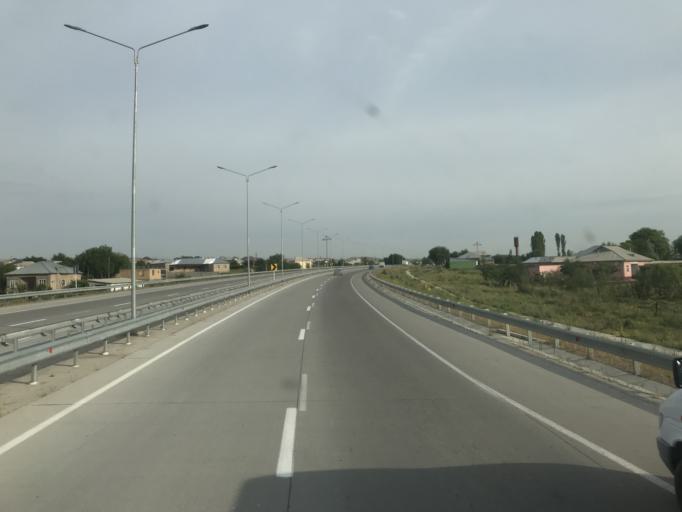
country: KZ
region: Ongtustik Qazaqstan
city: Qazyqurt
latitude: 41.7865
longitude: 69.3950
